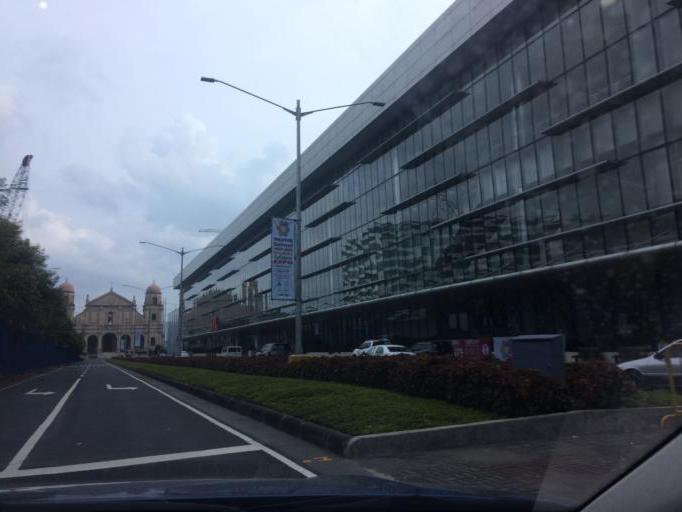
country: PH
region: Metro Manila
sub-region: City of Manila
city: Port Area
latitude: 14.5330
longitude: 120.9819
